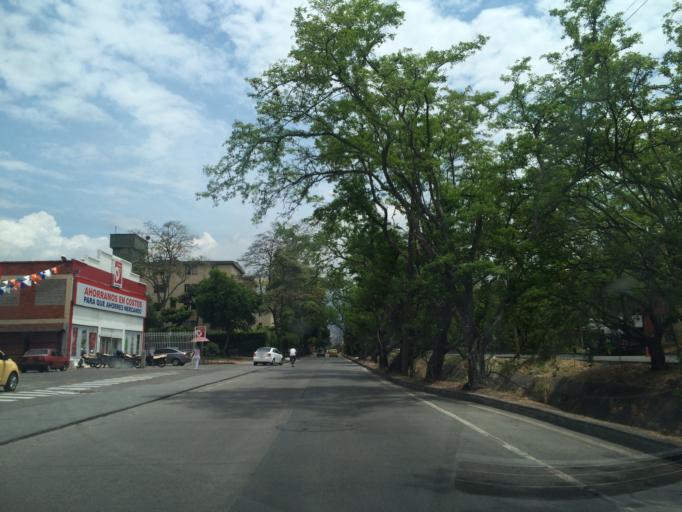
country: CO
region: Valle del Cauca
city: Cali
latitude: 3.4182
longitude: -76.5277
